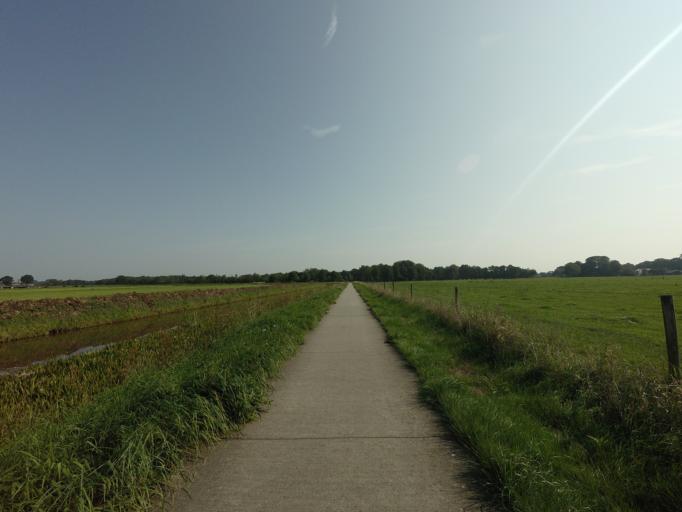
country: NL
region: Groningen
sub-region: Gemeente Groningen
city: Groningen
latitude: 53.1590
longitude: 6.5393
